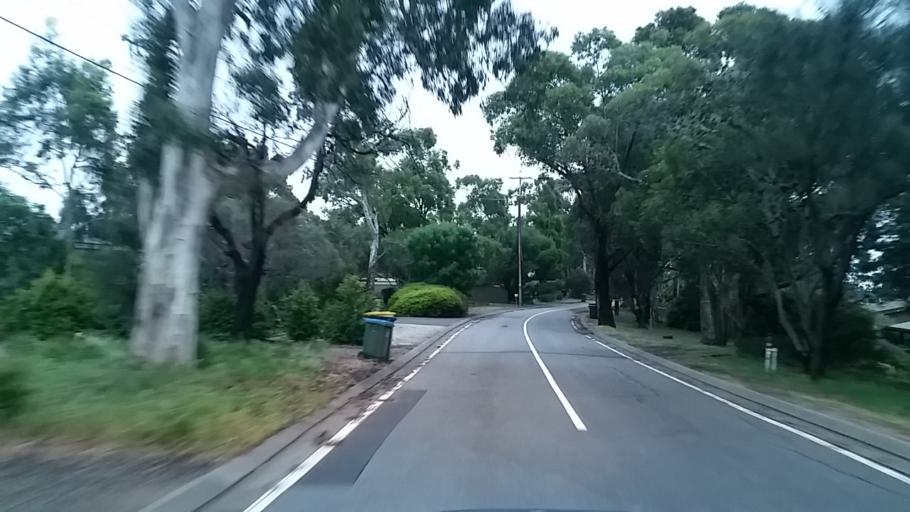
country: AU
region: South Australia
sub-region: Burnside
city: Wattle Park
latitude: -34.9533
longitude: 138.6985
